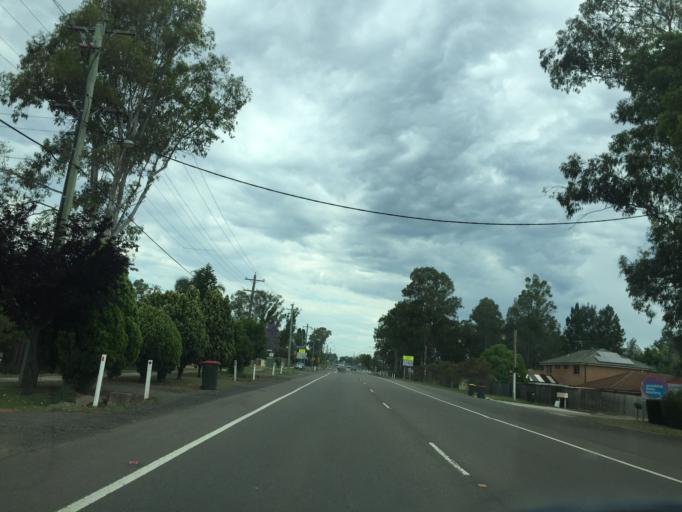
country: AU
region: New South Wales
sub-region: Blacktown
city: Glendenning
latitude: -33.7471
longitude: 150.8422
